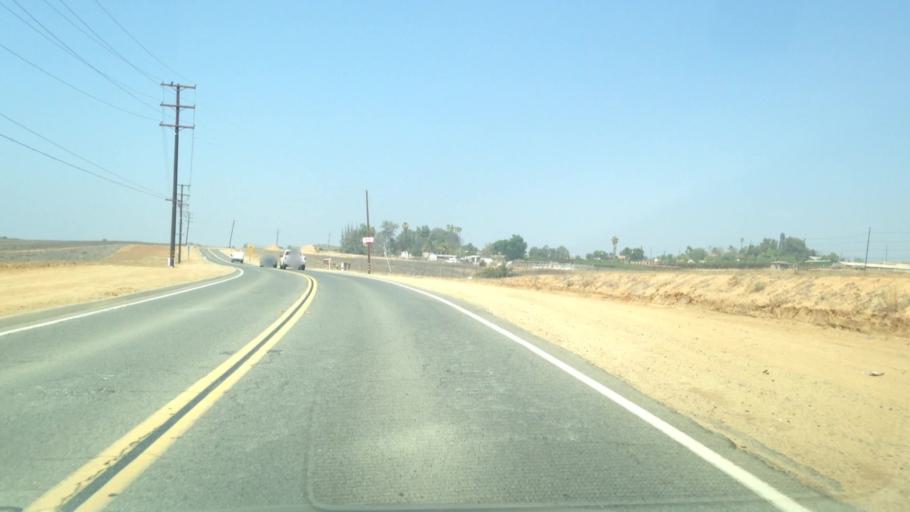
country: US
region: California
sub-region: Riverside County
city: Woodcrest
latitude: 33.8523
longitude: -117.3914
